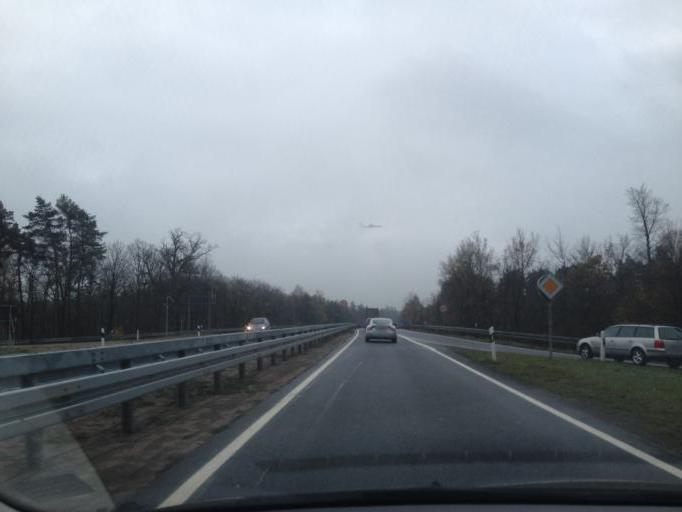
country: DE
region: Bavaria
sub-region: Regierungsbezirk Mittelfranken
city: Heroldsberg
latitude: 49.5012
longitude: 11.1341
